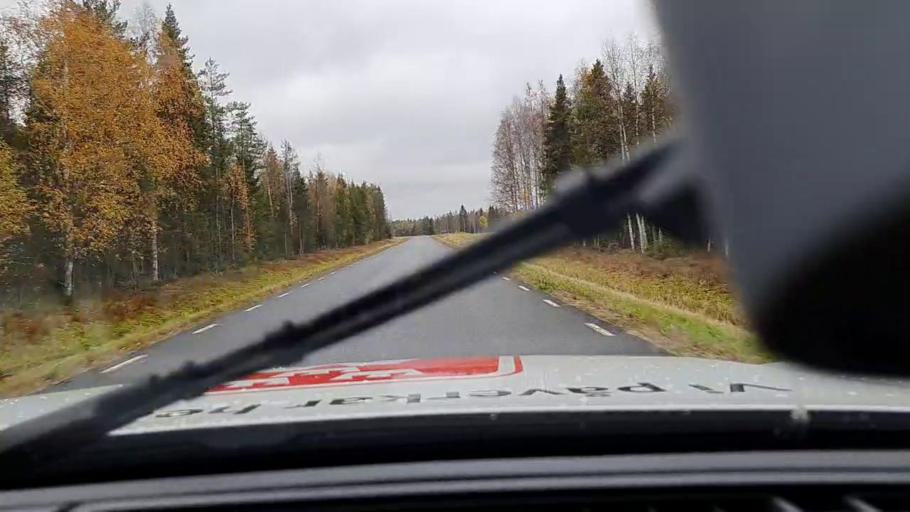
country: SE
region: Norrbotten
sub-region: Haparanda Kommun
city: Haparanda
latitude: 65.9300
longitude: 23.8169
